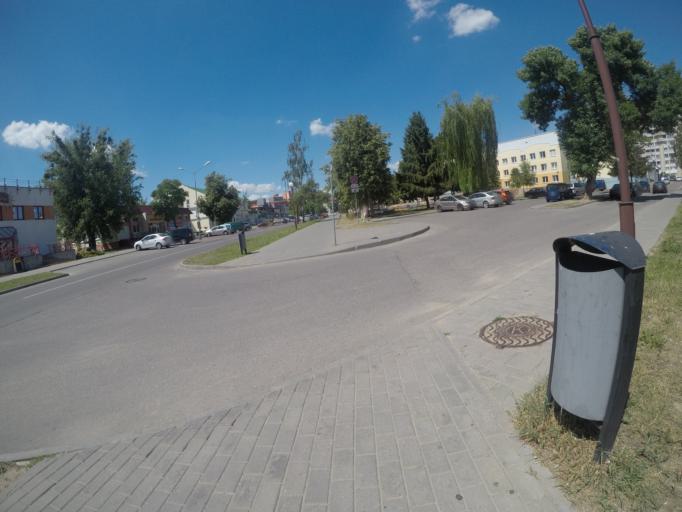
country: BY
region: Grodnenskaya
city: Hrodna
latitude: 53.6931
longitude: 23.8290
